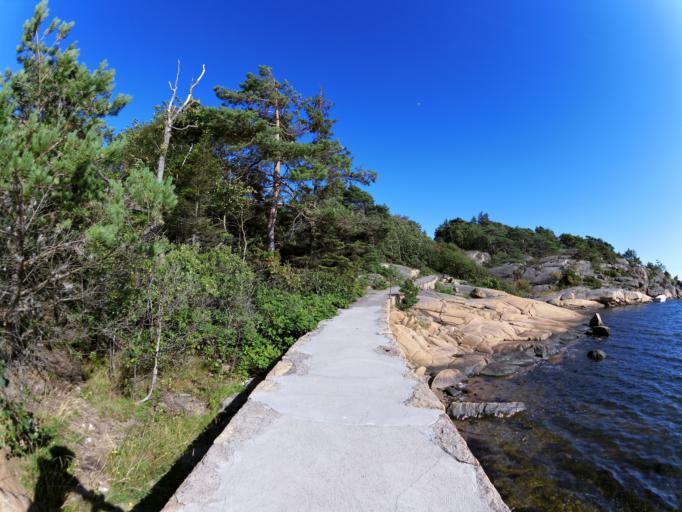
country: NO
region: Ostfold
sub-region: Fredrikstad
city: Fredrikstad
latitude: 59.1659
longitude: 10.8359
